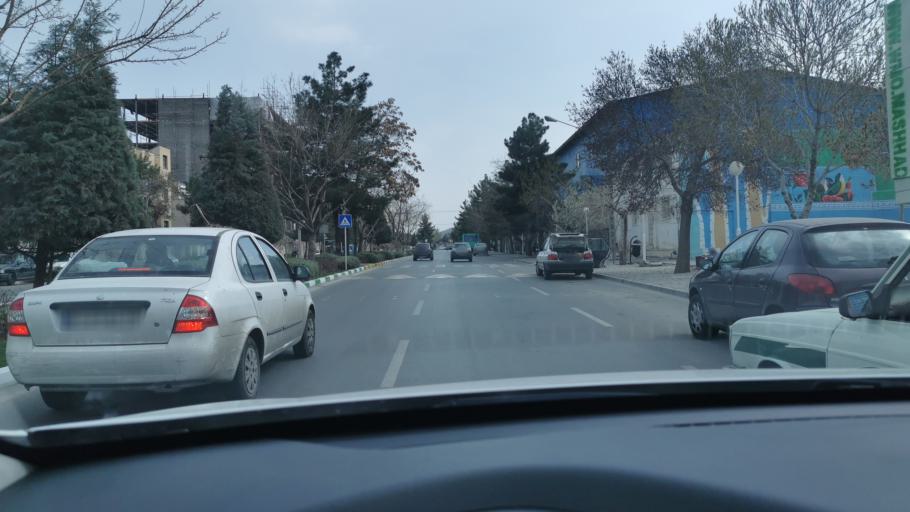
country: IR
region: Razavi Khorasan
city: Mashhad
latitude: 36.2790
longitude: 59.5649
